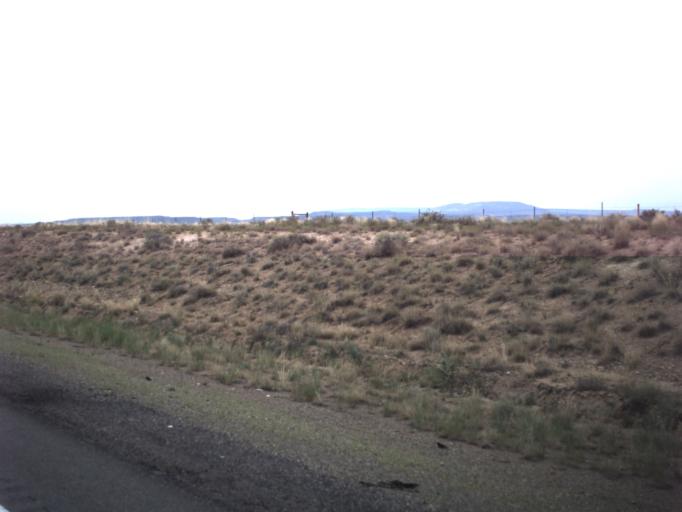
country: US
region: Utah
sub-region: Carbon County
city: East Carbon City
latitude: 39.5035
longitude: -110.5302
